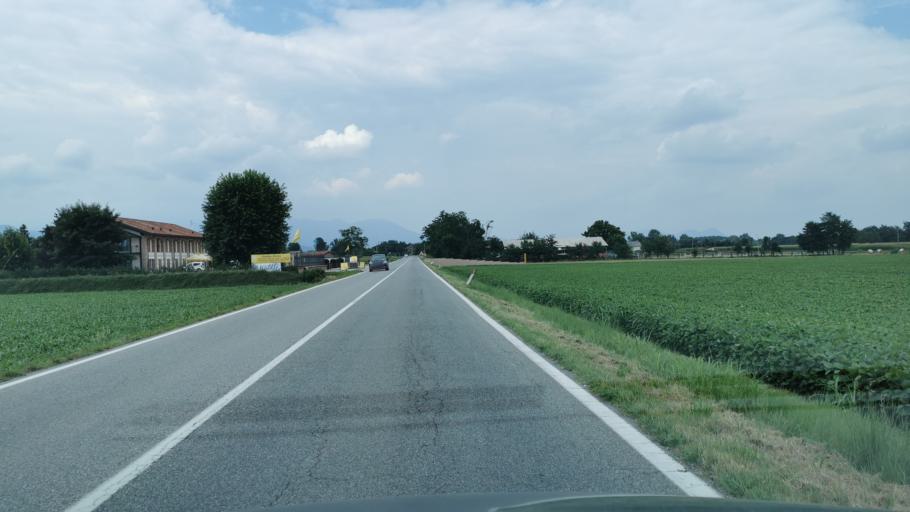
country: IT
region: Piedmont
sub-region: Provincia di Torino
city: Garzigliana
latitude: 44.8197
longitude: 7.3708
